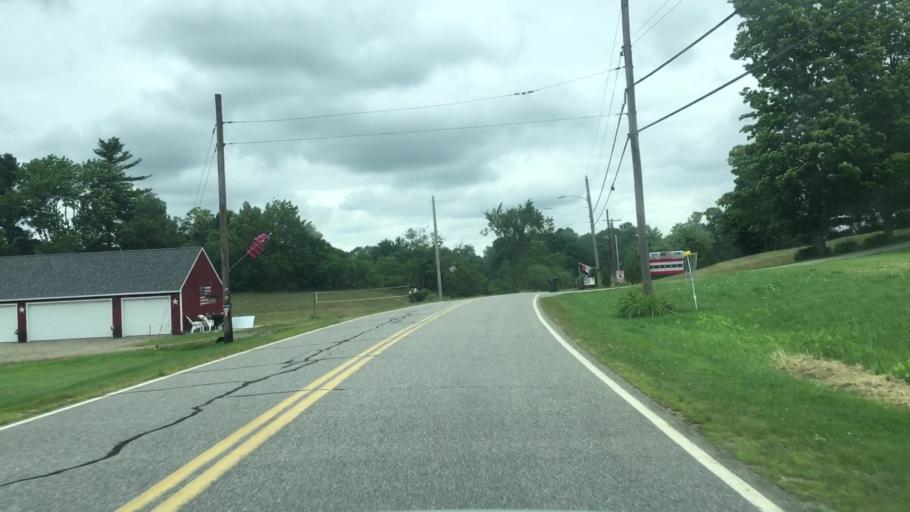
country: US
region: Maine
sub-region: York County
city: Biddeford
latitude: 43.5167
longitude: -70.5127
